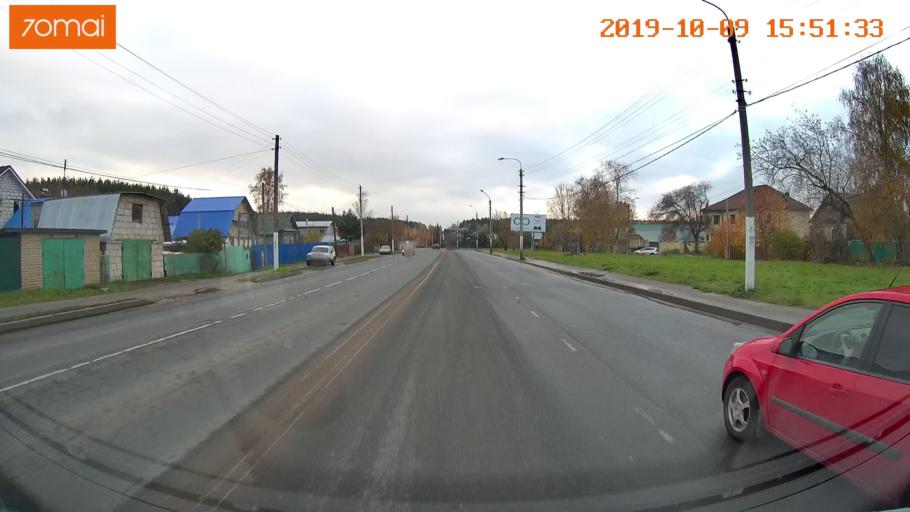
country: RU
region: Kostroma
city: Oktyabr'skiy
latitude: 57.7970
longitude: 40.9786
